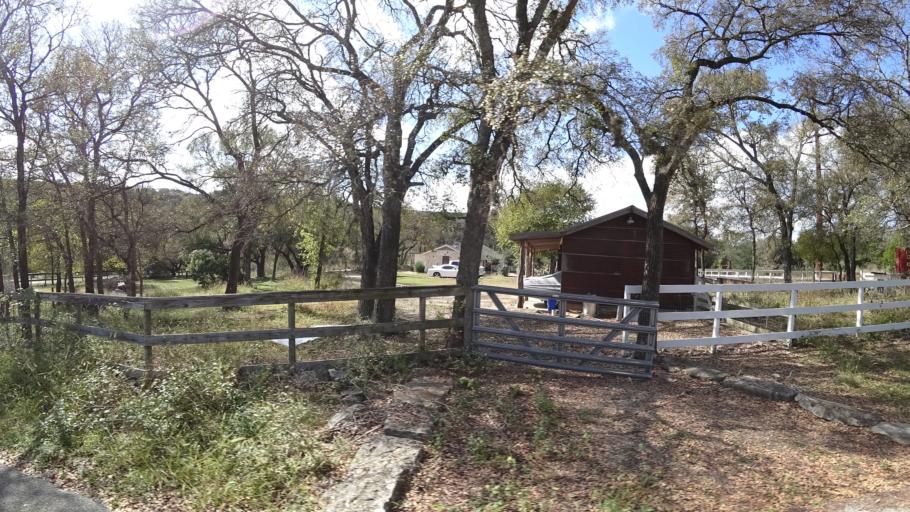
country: US
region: Texas
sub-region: Williamson County
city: Jollyville
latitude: 30.4003
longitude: -97.7820
